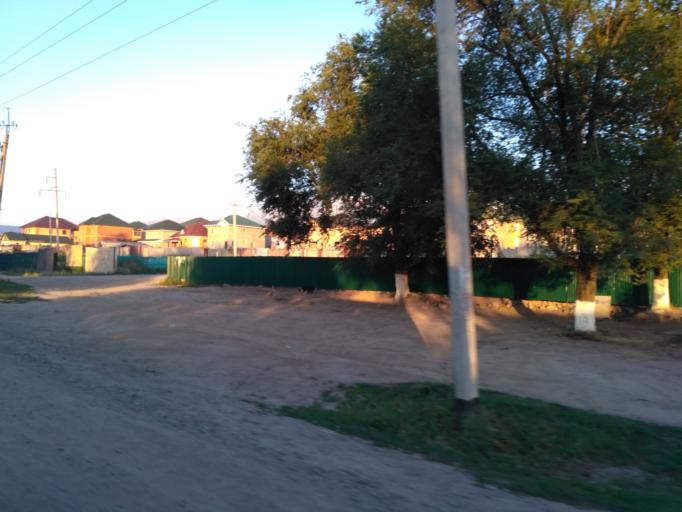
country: KZ
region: Almaty Qalasy
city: Almaty
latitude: 43.1733
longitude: 76.7814
